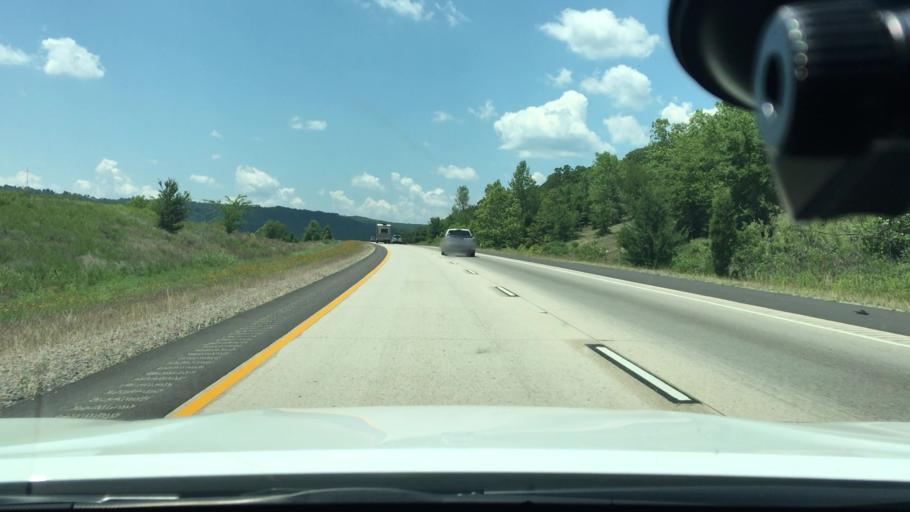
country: US
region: Arkansas
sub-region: Crawford County
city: Cedarville
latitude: 35.6968
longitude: -94.1861
